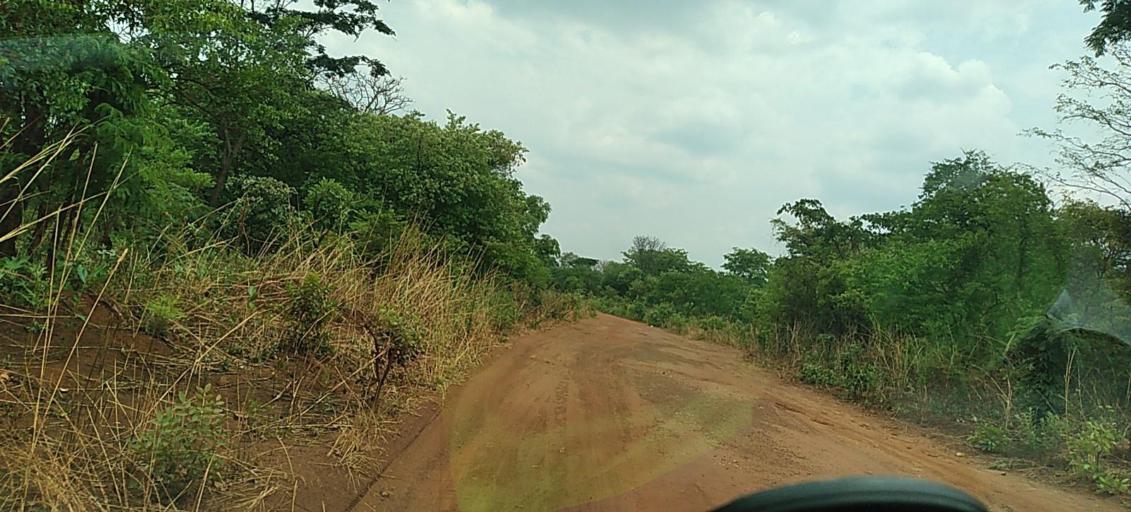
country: ZM
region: North-Western
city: Kansanshi
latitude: -12.0481
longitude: 26.3797
